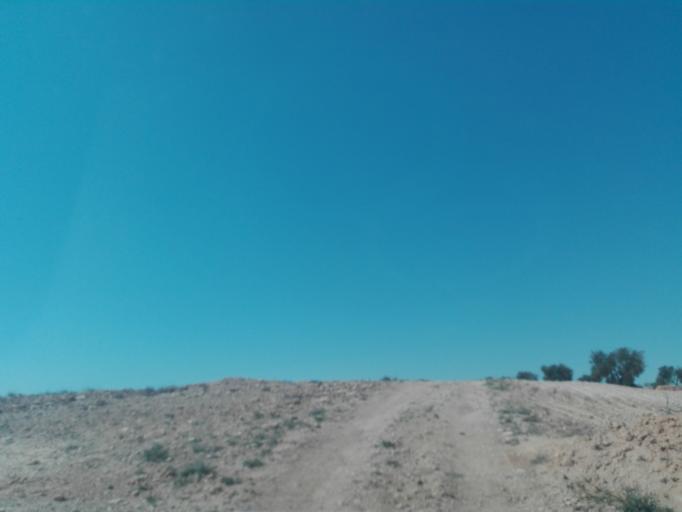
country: TN
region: Safaqis
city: Bi'r `Ali Bin Khalifah
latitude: 34.7949
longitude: 10.2827
